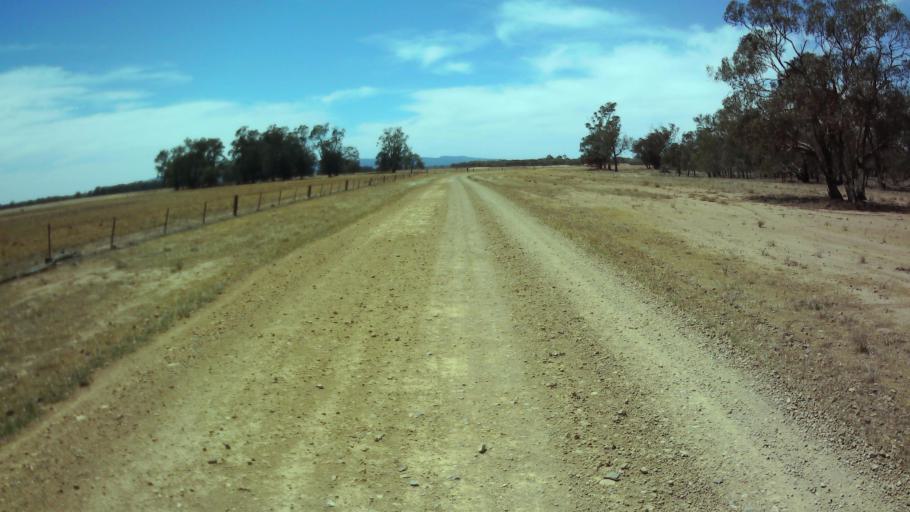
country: AU
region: New South Wales
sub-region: Weddin
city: Grenfell
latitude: -33.8621
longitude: 147.7574
